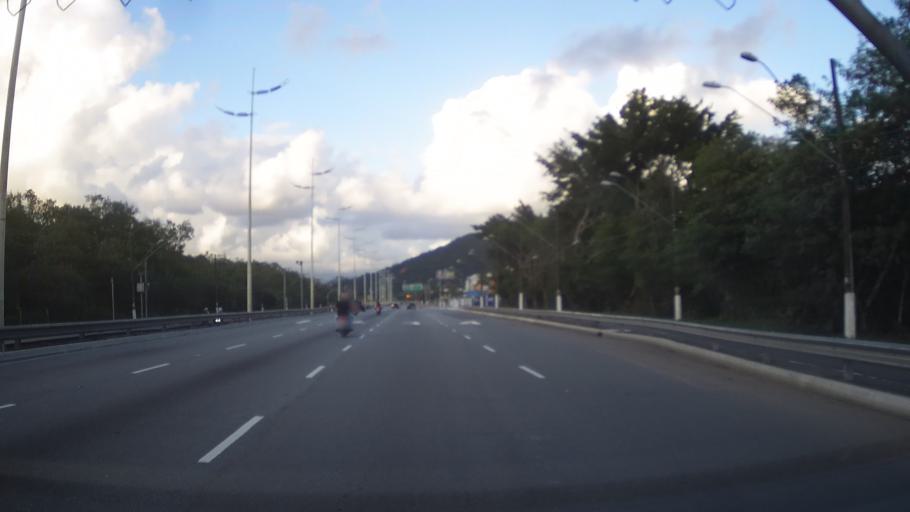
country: BR
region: Sao Paulo
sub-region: Praia Grande
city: Praia Grande
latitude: -23.9937
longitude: -46.4028
